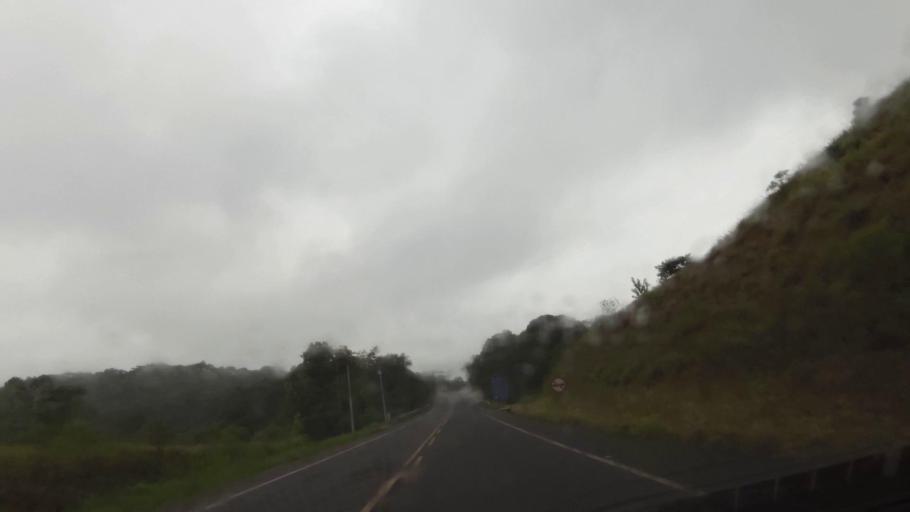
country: BR
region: Espirito Santo
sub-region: Guarapari
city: Guarapari
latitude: -20.6371
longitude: -40.5285
